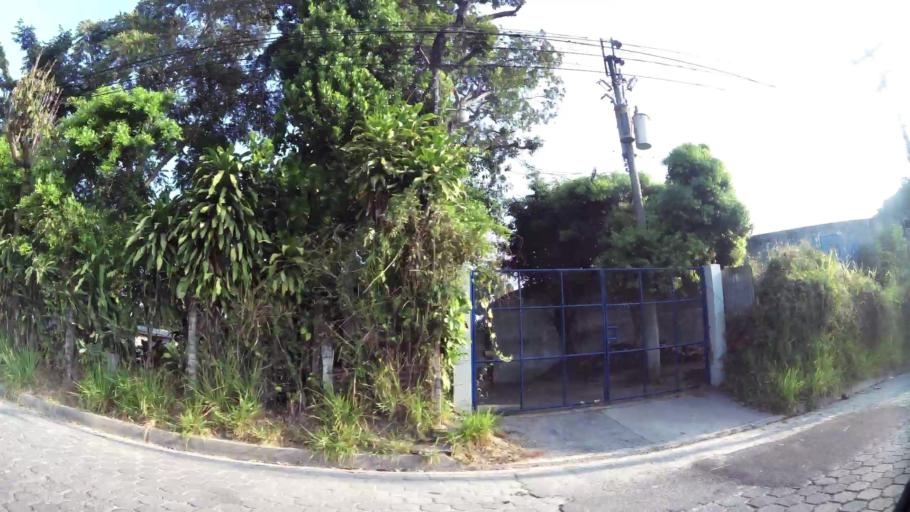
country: SV
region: San Salvador
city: San Salvador
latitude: 13.6812
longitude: -89.2052
